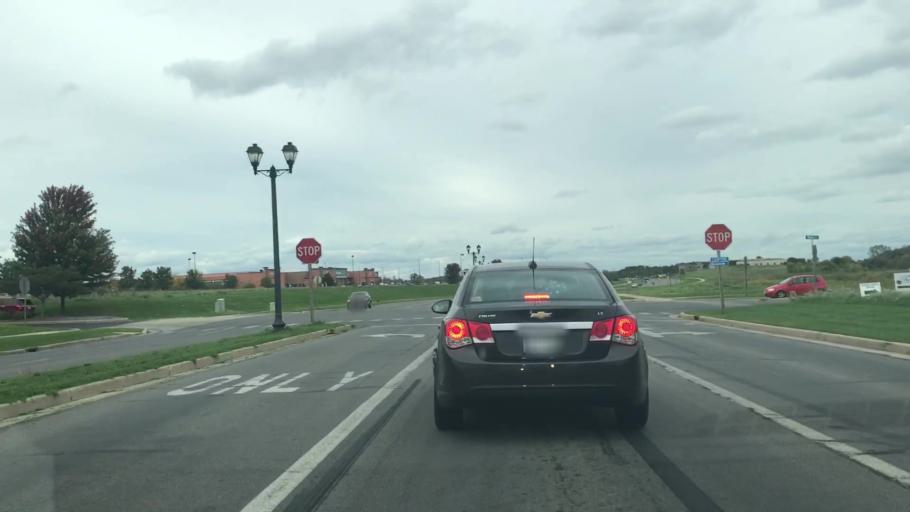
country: US
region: Wisconsin
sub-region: Waukesha County
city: Mukwonago
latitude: 42.8504
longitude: -88.3174
